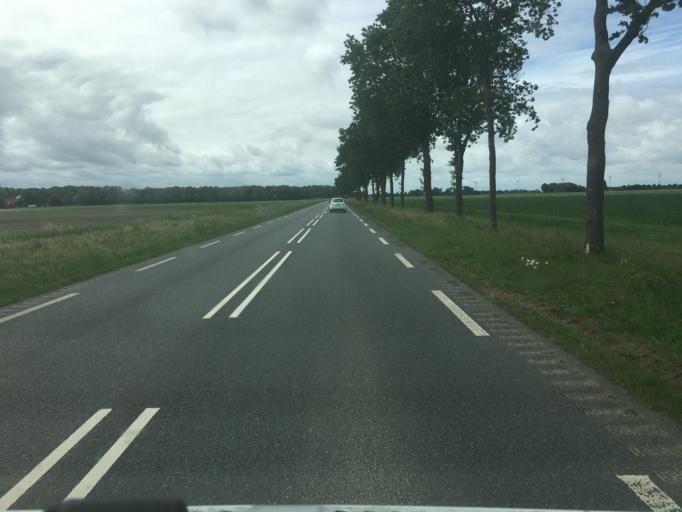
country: NL
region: Flevoland
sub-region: Gemeente Noordoostpolder
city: Emmeloord
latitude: 52.6586
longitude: 5.7318
